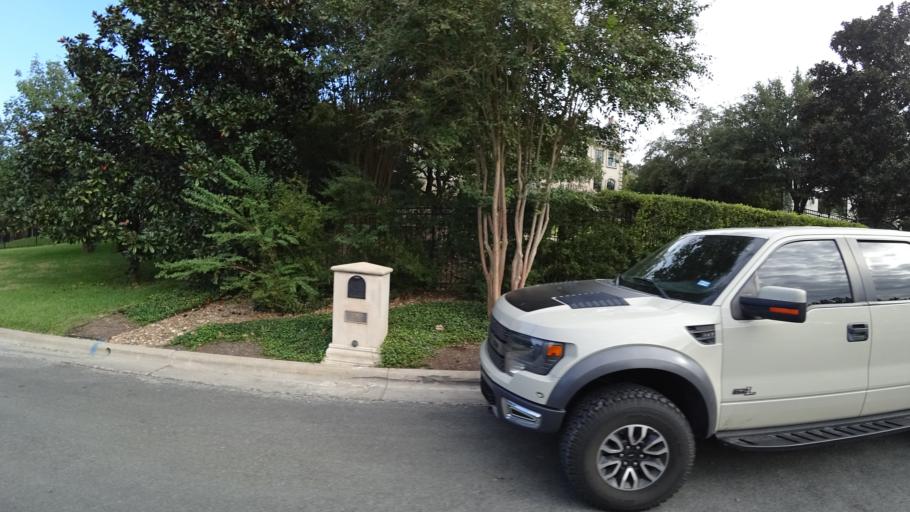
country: US
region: Texas
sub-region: Travis County
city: Rollingwood
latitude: 30.2864
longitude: -97.7922
